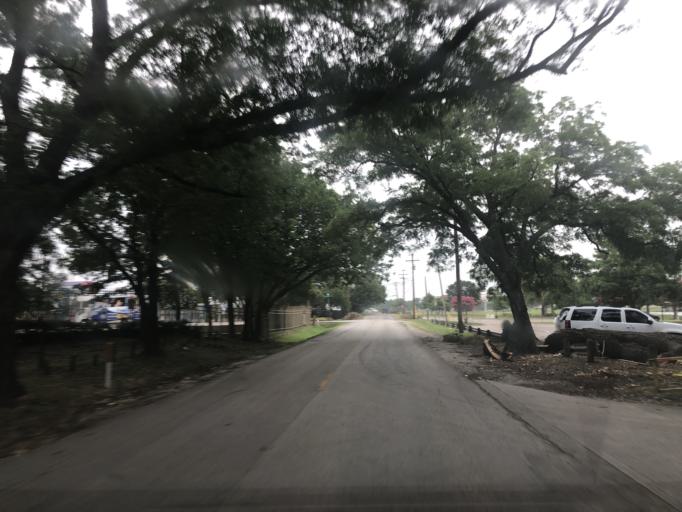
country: US
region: Texas
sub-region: Dallas County
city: University Park
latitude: 32.8539
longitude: -96.8693
